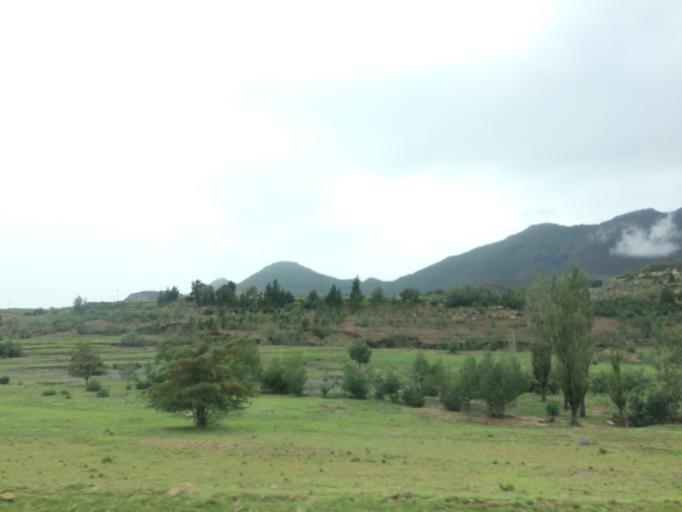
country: LS
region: Mafeteng
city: Mafeteng
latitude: -29.7828
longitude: 27.5220
